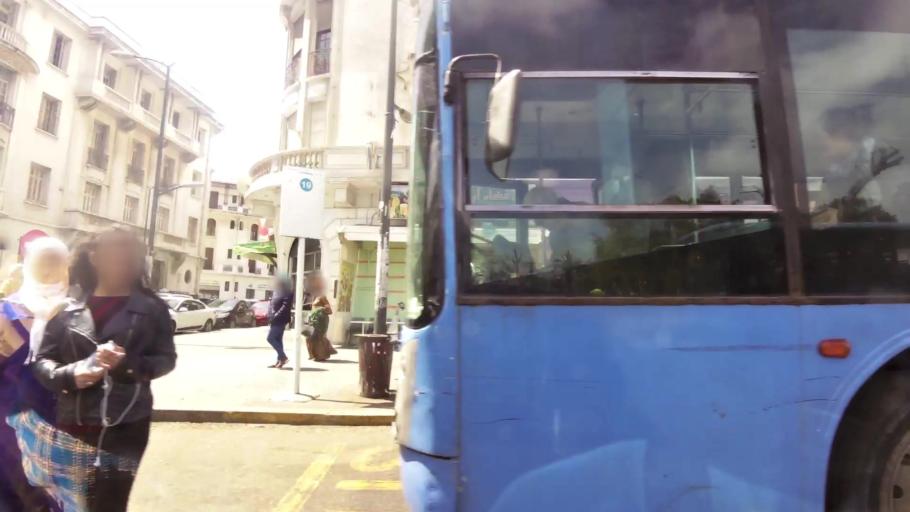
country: MA
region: Grand Casablanca
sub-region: Casablanca
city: Casablanca
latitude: 33.5943
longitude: -7.6193
